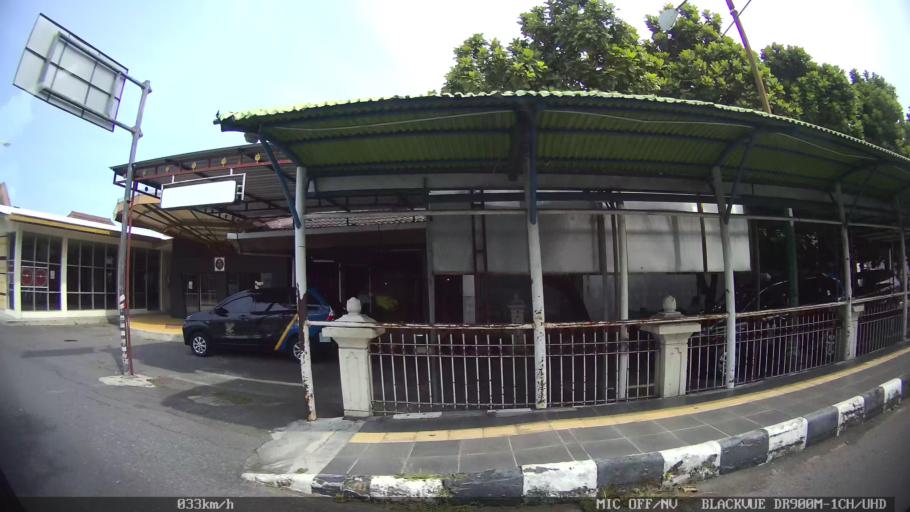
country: ID
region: Daerah Istimewa Yogyakarta
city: Depok
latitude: -7.7853
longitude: 110.4368
